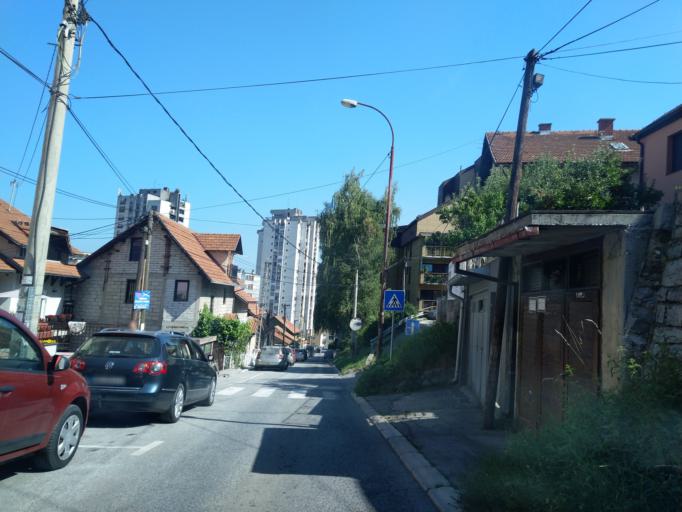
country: RS
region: Central Serbia
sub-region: Zlatiborski Okrug
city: Uzice
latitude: 43.8567
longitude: 19.8319
